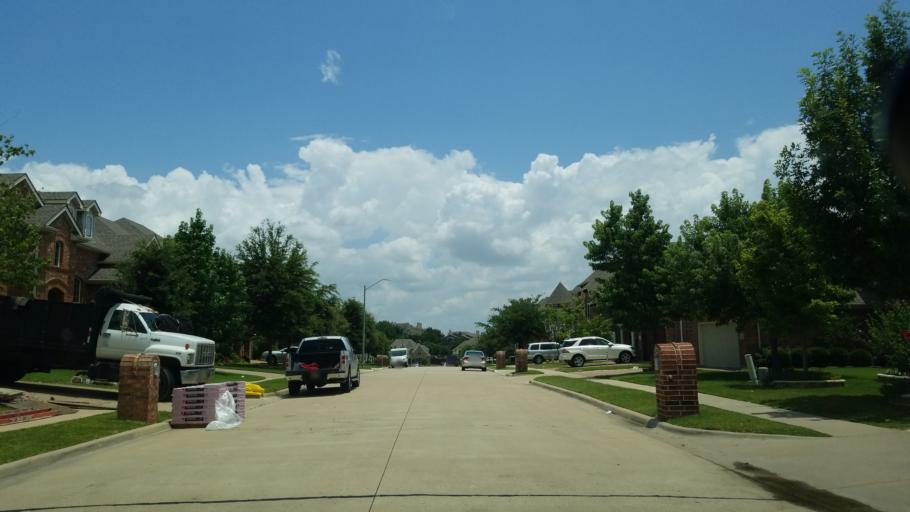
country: US
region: Texas
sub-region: Dallas County
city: Coppell
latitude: 32.9429
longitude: -96.9630
